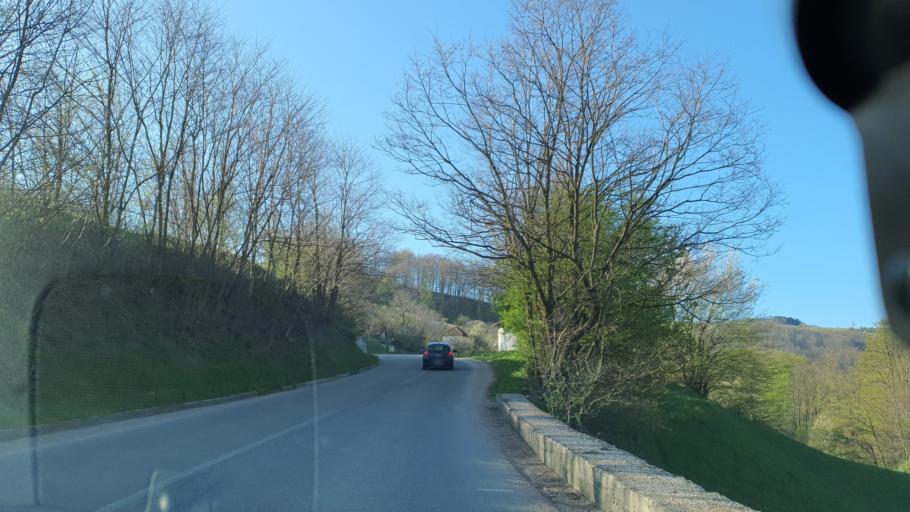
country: RS
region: Central Serbia
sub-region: Kolubarski Okrug
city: Osecina
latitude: 44.2742
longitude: 19.5227
